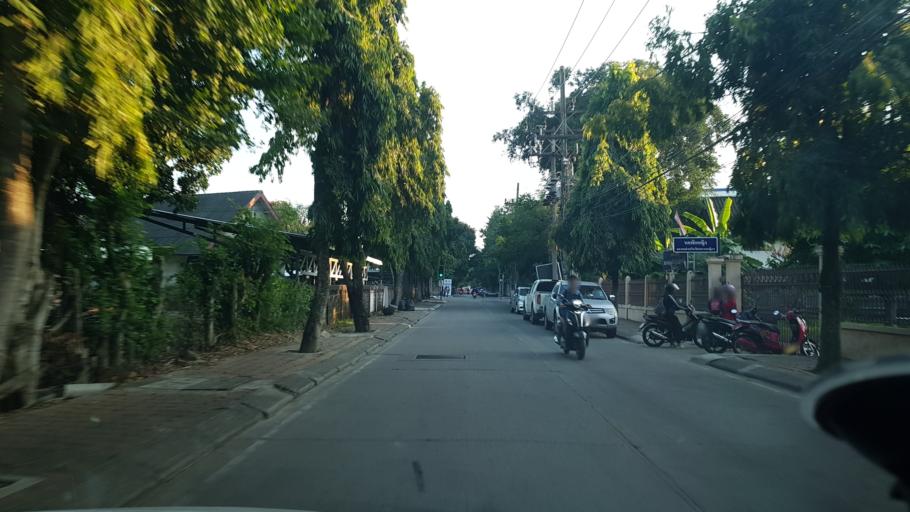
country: TH
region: Chiang Rai
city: Chiang Rai
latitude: 19.9121
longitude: 99.8347
